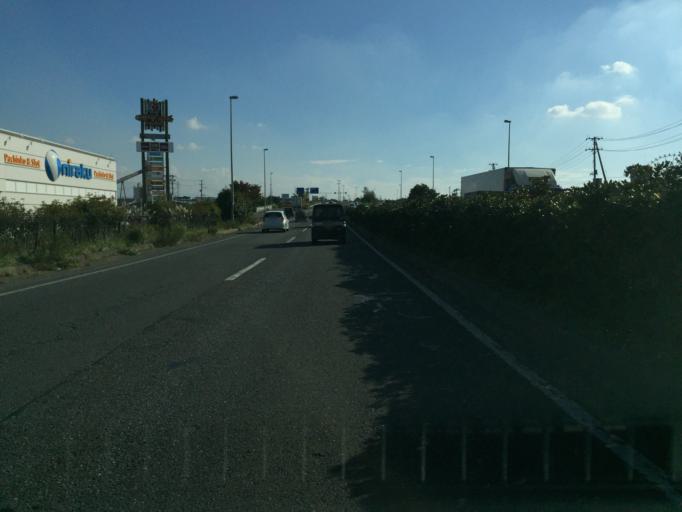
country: JP
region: Fukushima
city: Koriyama
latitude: 37.4481
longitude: 140.3792
